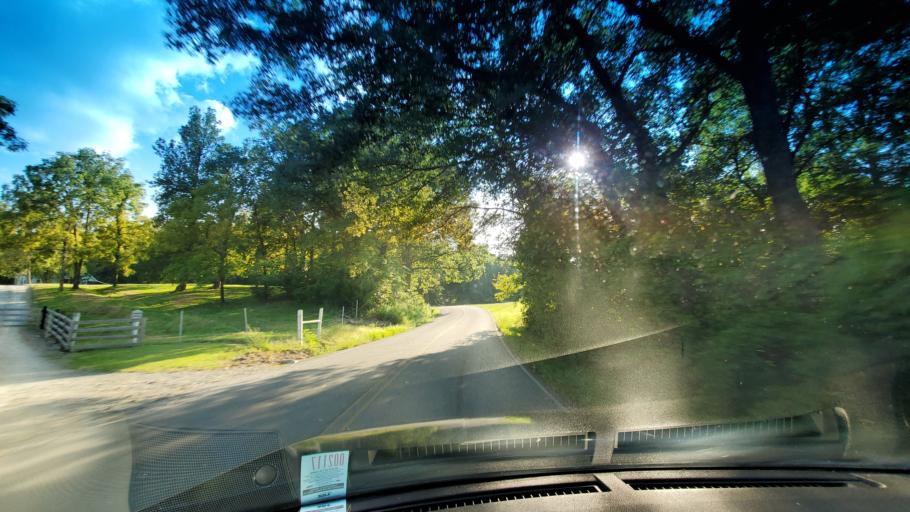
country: US
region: Tennessee
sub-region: Wilson County
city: Lebanon
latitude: 36.1577
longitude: -86.3745
